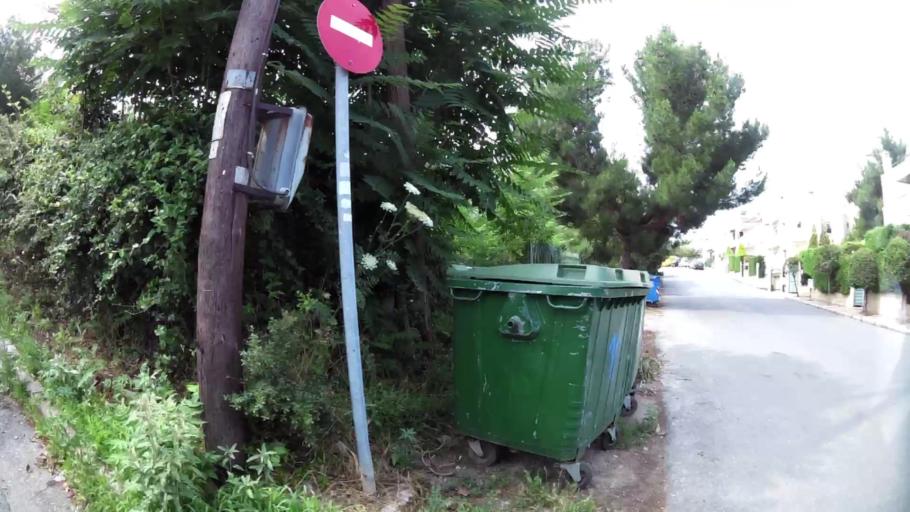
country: GR
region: Central Macedonia
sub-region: Nomos Thessalonikis
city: Panorama
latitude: 40.5808
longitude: 23.0272
